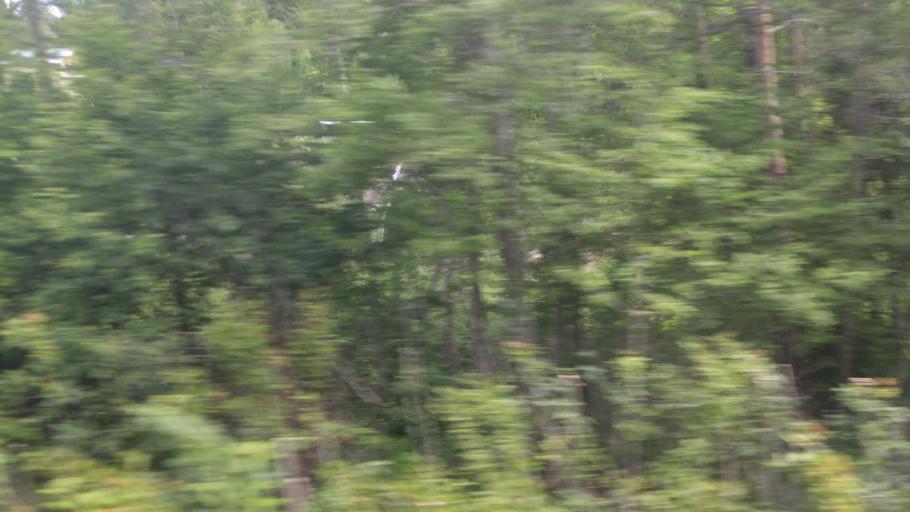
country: NO
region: Sor-Trondelag
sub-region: Midtre Gauldal
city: Storen
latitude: 63.0334
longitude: 10.3088
